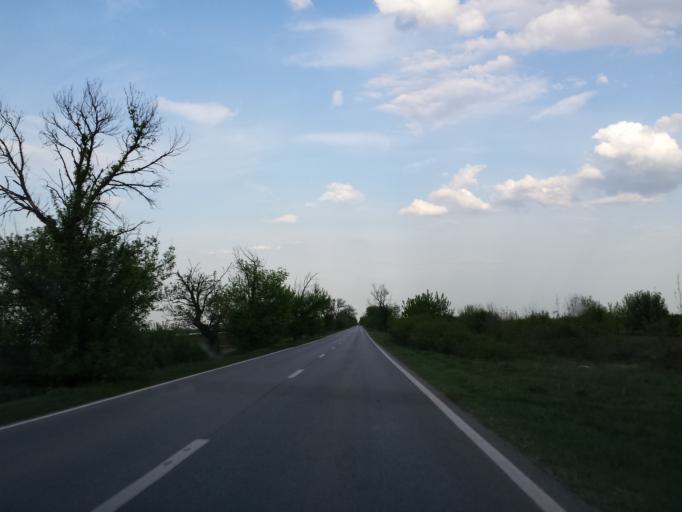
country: RO
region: Timis
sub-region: Comuna Gottlob
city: Gottlob
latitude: 45.9659
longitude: 20.7217
